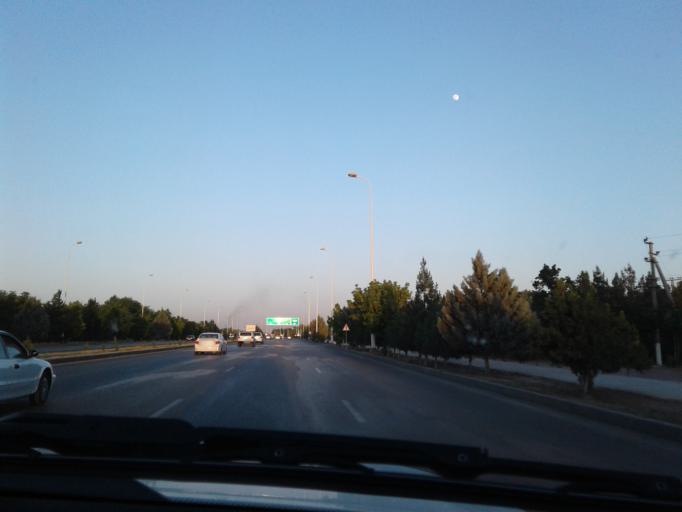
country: TM
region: Ahal
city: Abadan
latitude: 38.0269
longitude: 58.2381
